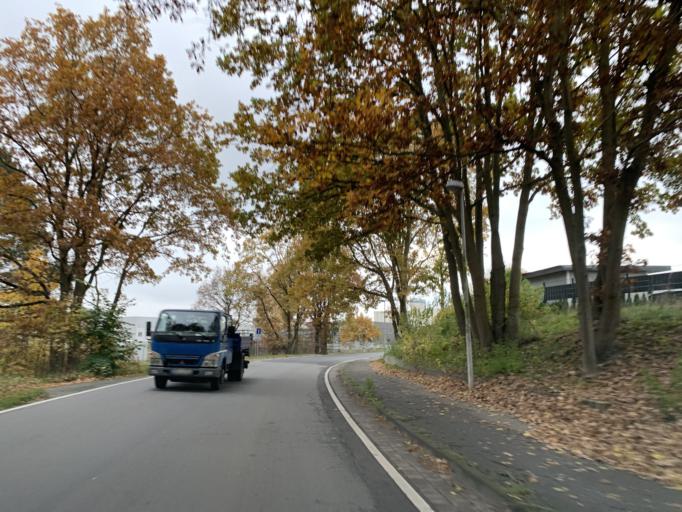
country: DE
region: Mecklenburg-Vorpommern
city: Trollenhagen
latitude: 53.5802
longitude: 13.3092
